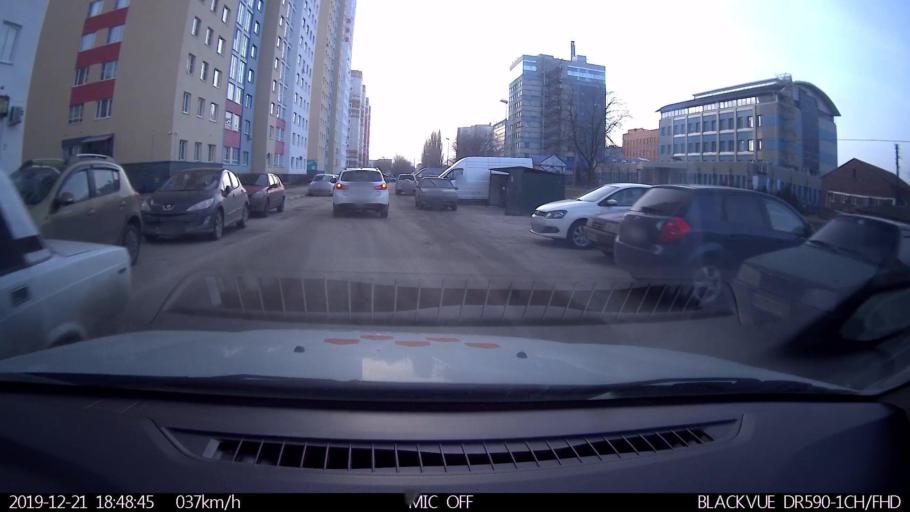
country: RU
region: Nizjnij Novgorod
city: Nizhniy Novgorod
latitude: 56.3248
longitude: 43.9298
